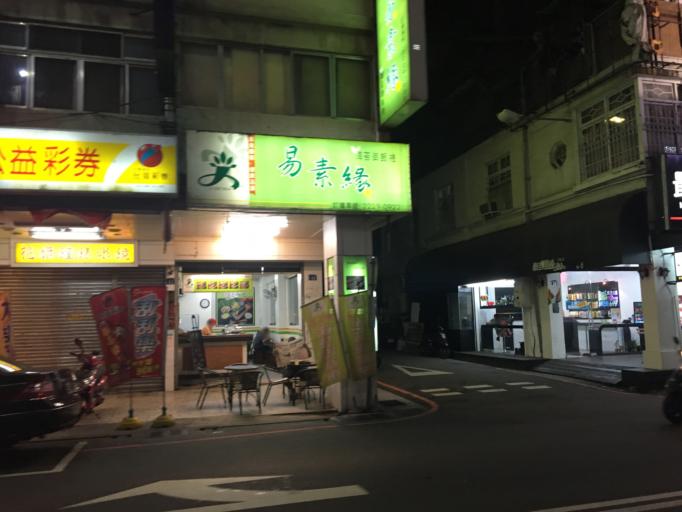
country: TW
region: Taiwan
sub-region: Taichung City
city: Taichung
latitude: 24.1347
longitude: 120.6827
